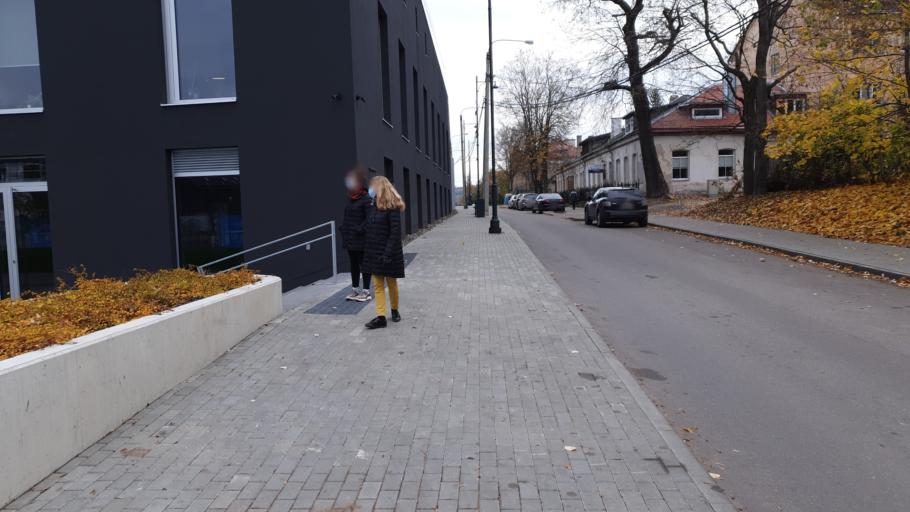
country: LT
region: Vilnius County
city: Rasos
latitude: 54.6785
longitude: 25.3022
